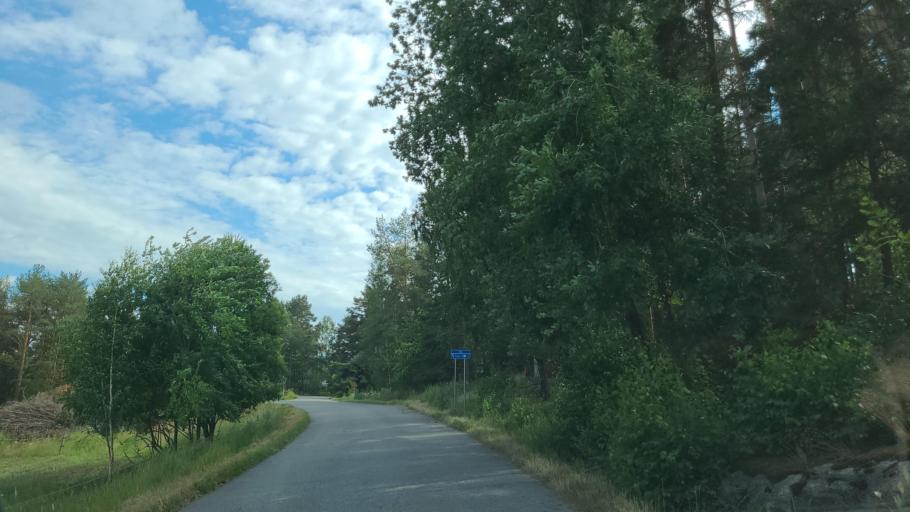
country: FI
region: Varsinais-Suomi
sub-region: Turku
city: Rymaettylae
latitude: 60.2946
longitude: 21.9370
